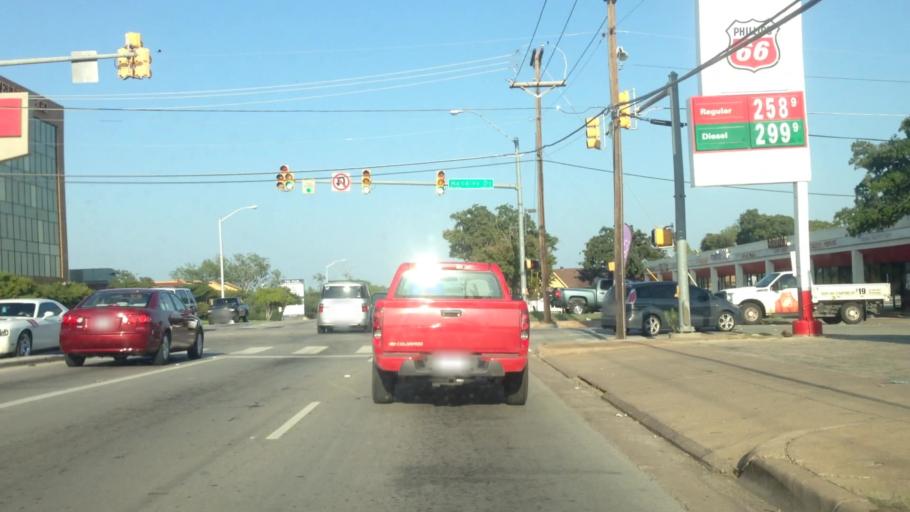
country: US
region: Texas
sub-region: Tarrant County
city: Richland Hills
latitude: 32.7543
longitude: -97.2151
